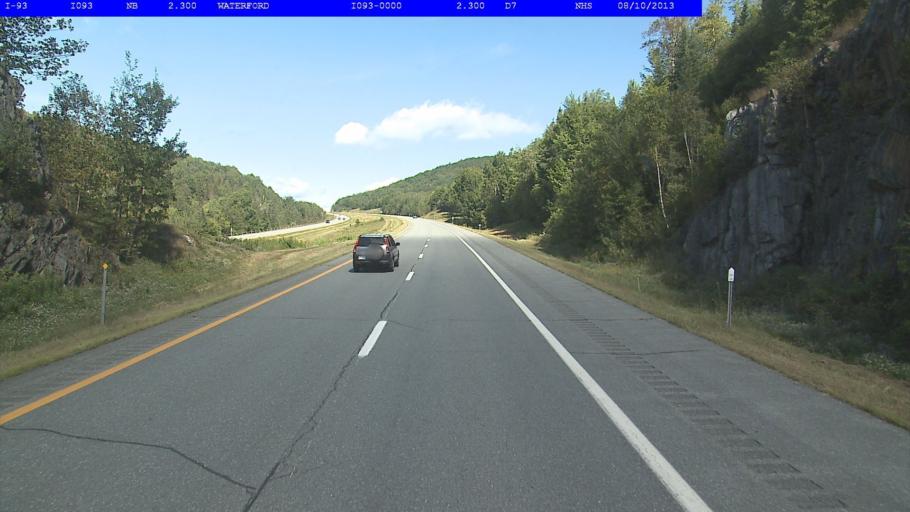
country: US
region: Vermont
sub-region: Caledonia County
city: Saint Johnsbury
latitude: 44.3737
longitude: -71.9082
